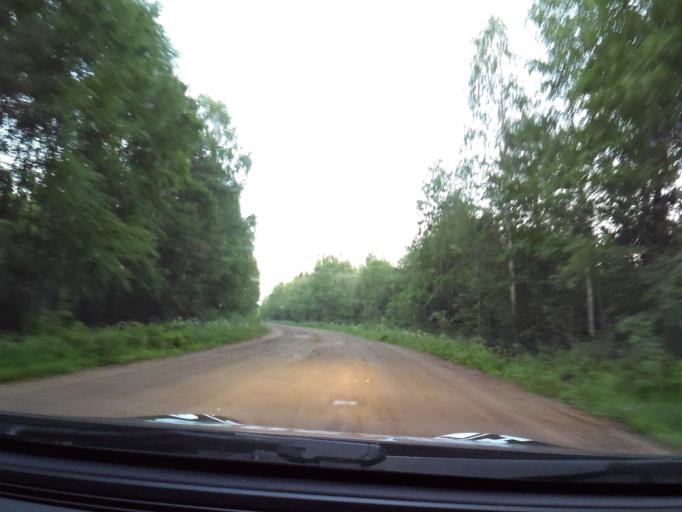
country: RU
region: Leningrad
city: Voznesen'ye
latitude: 60.8536
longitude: 35.8898
